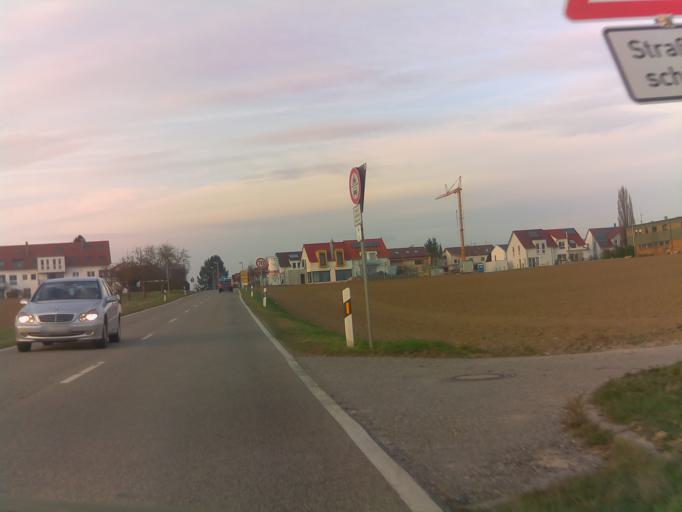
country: DE
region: Baden-Wuerttemberg
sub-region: Regierungsbezirk Stuttgart
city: Hemmingen
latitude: 48.8590
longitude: 9.0284
